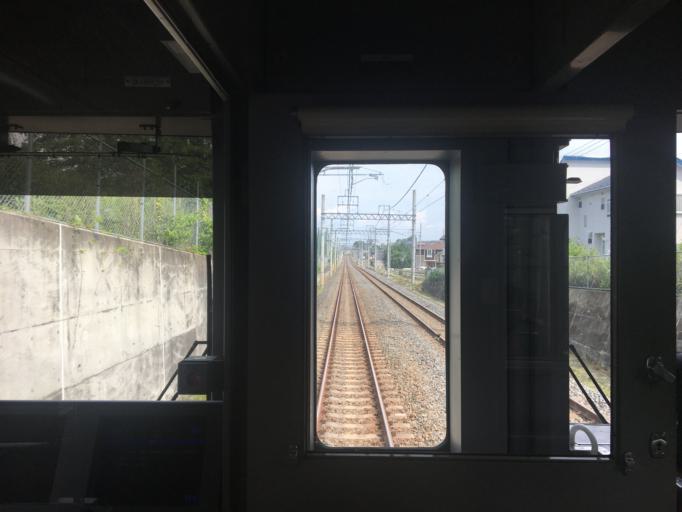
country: JP
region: Saitama
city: Ogawa
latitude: 36.0486
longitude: 139.3190
